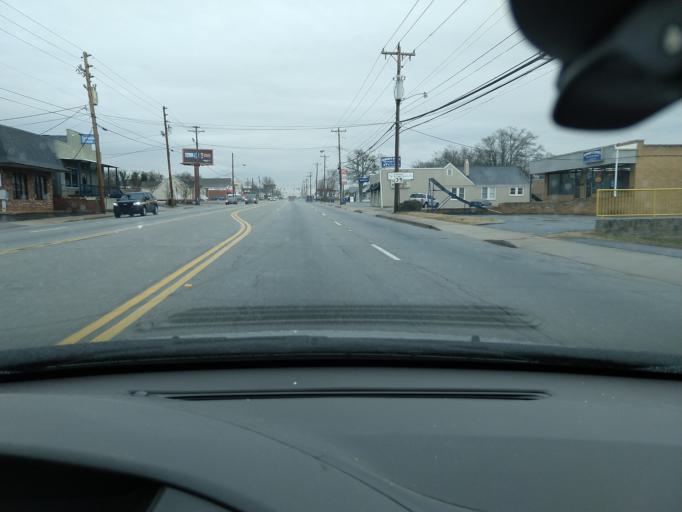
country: US
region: South Carolina
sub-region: Greenville County
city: Greenville
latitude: 34.8463
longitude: -82.3680
